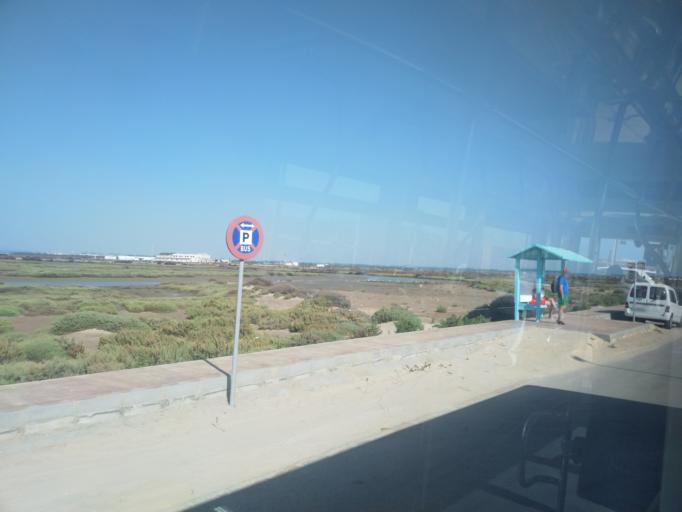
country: ES
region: Andalusia
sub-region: Provincia de Cadiz
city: San Fernando
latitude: 36.4222
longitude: -6.2257
